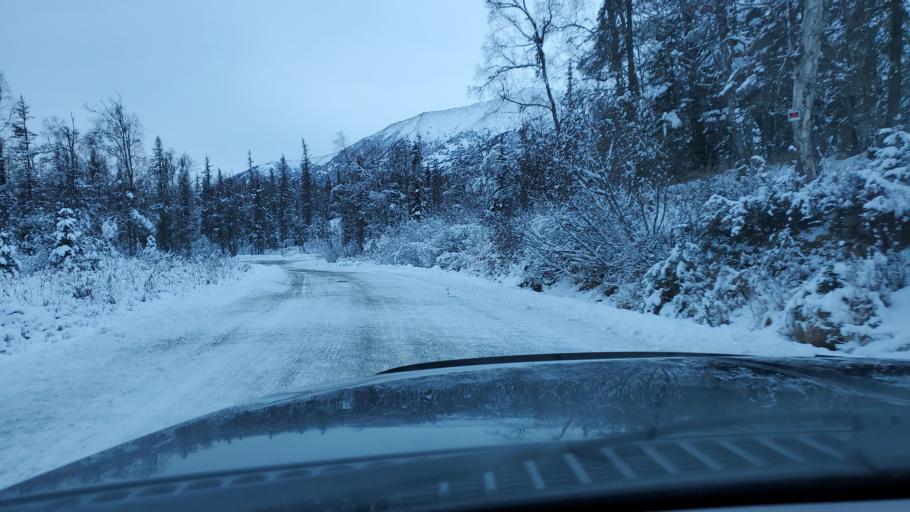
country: US
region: Alaska
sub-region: Matanuska-Susitna Borough
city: Lakes
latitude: 61.6968
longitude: -149.3236
